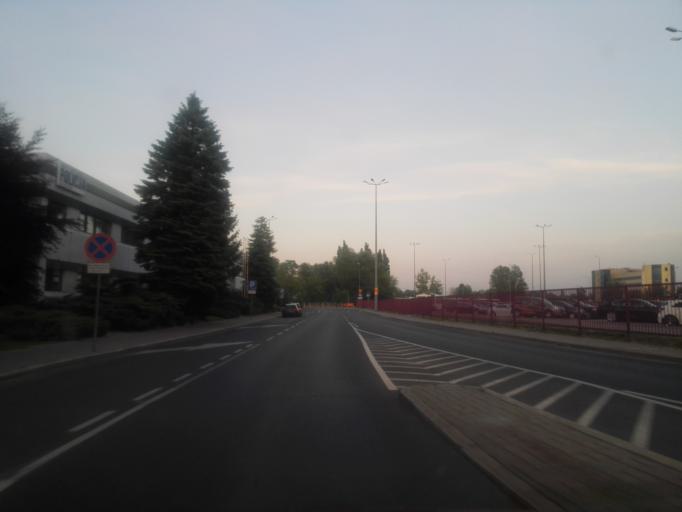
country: PL
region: Masovian Voivodeship
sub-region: Warszawa
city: Wlochy
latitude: 52.1701
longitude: 20.9760
